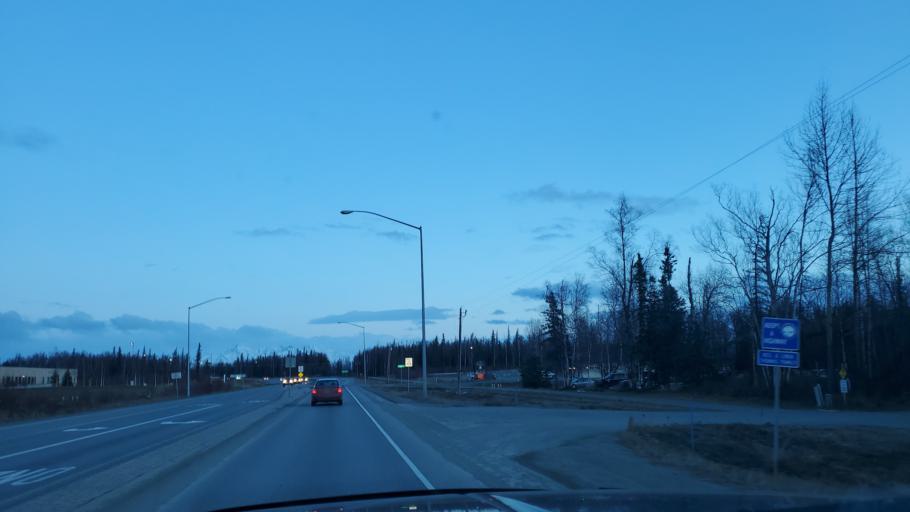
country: US
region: Alaska
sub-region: Matanuska-Susitna Borough
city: Wasilla
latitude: 61.5705
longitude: -149.4435
